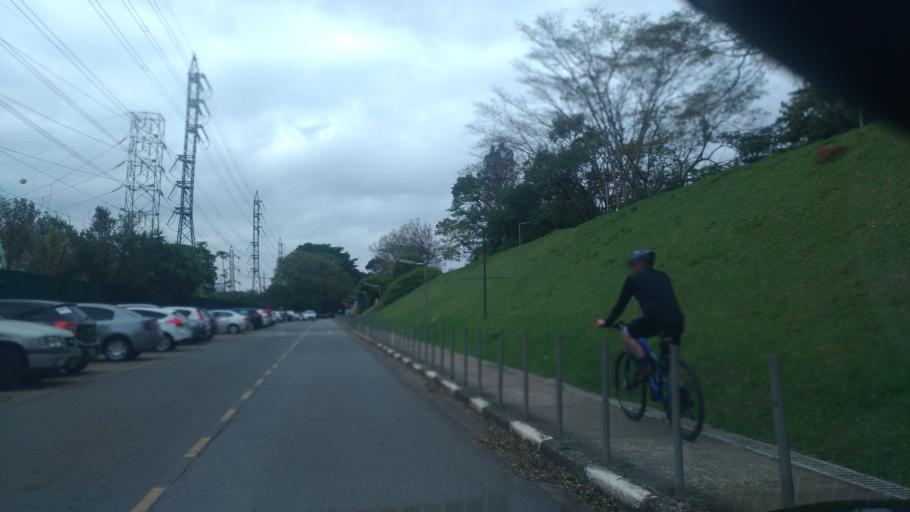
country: BR
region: Sao Paulo
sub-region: Osasco
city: Osasco
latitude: -23.5461
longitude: -46.7185
